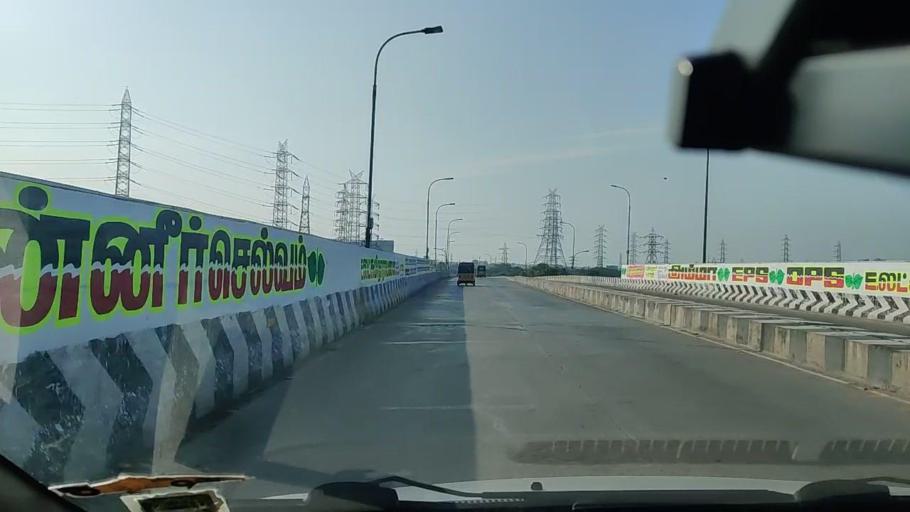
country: IN
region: Tamil Nadu
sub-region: Chennai
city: George Town
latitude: 13.1106
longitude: 80.2660
